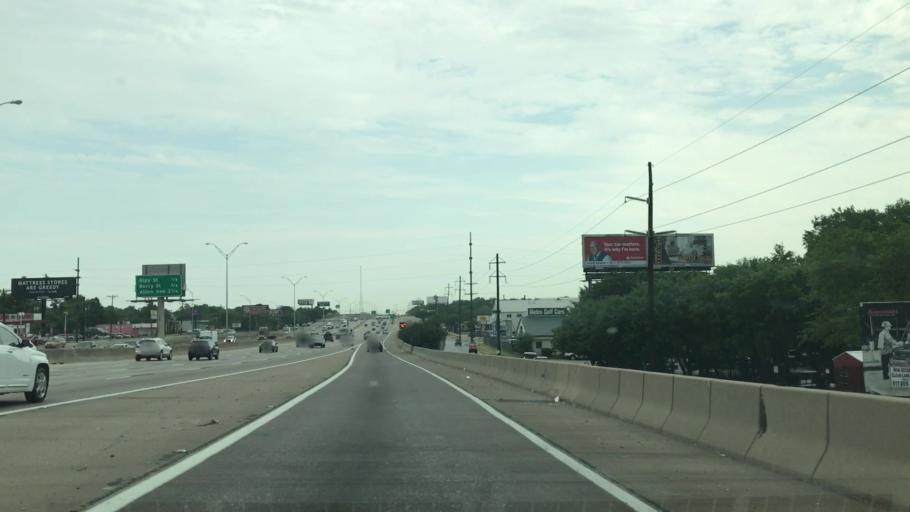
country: US
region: Texas
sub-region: Tarrant County
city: Edgecliff Village
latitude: 32.6877
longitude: -97.3204
